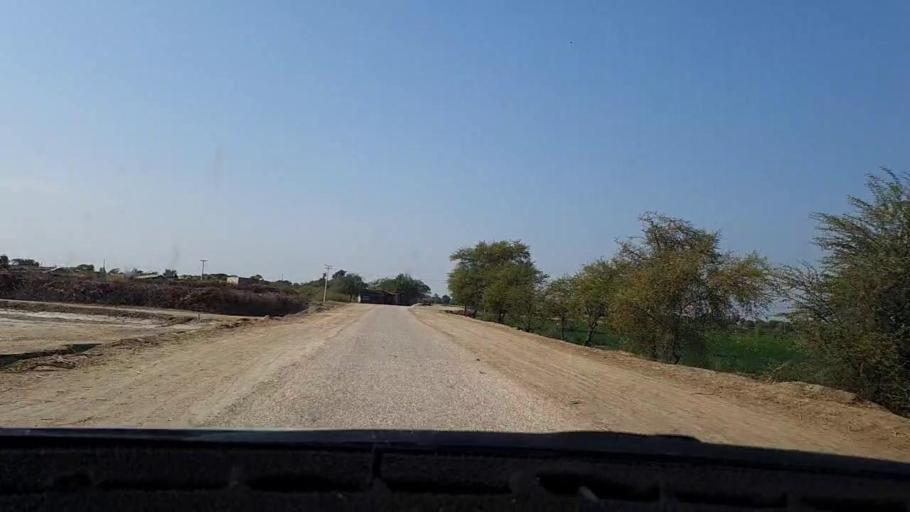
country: PK
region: Sindh
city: Tando Mittha Khan
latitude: 25.8113
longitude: 69.3163
